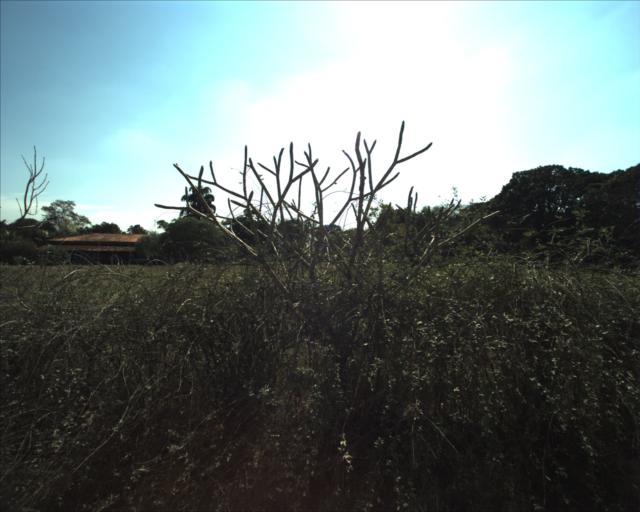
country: BR
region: Sao Paulo
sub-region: Aracoiaba Da Serra
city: Aracoiaba da Serra
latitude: -23.4873
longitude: -47.5447
